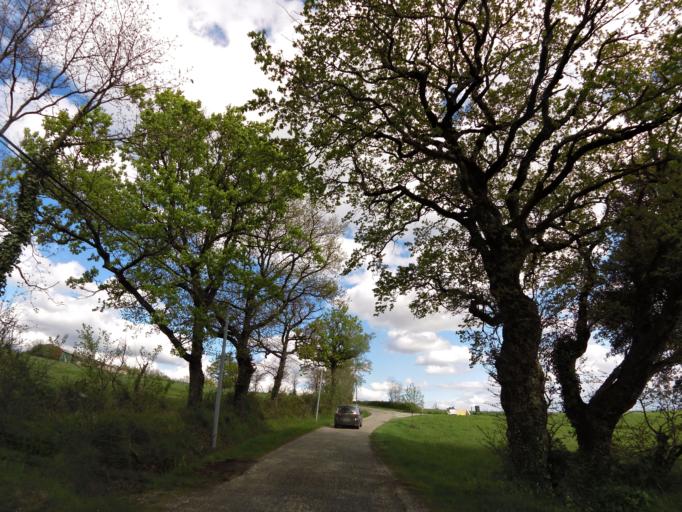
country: FR
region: Languedoc-Roussillon
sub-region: Departement de l'Aude
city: Saint-Martin-Lalande
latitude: 43.3680
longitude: 2.0625
